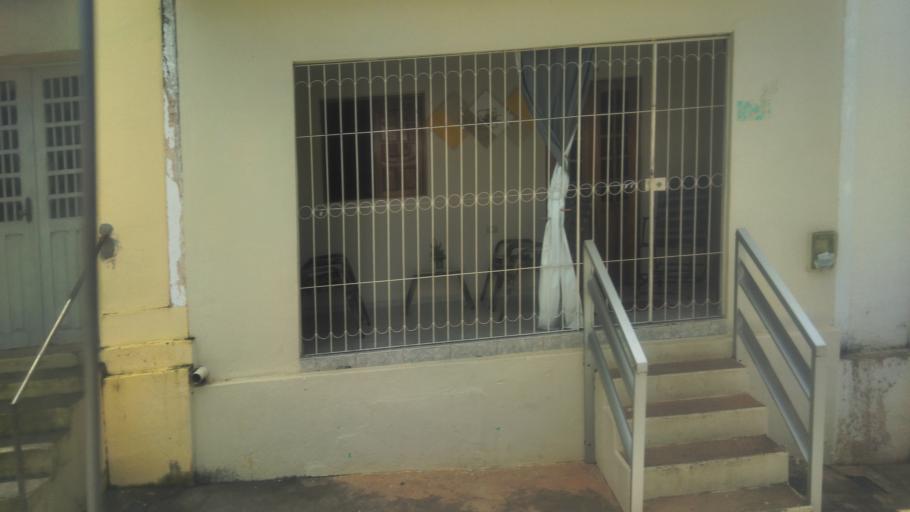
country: BR
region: Pernambuco
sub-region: Vicencia
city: Vicencia
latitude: -7.7255
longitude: -35.3253
